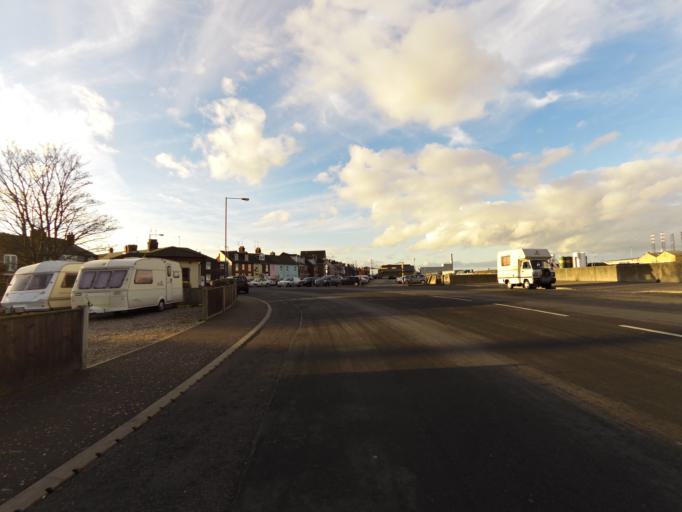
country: GB
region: England
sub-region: Norfolk
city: Gorleston-on-Sea
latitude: 52.5736
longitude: 1.7321
